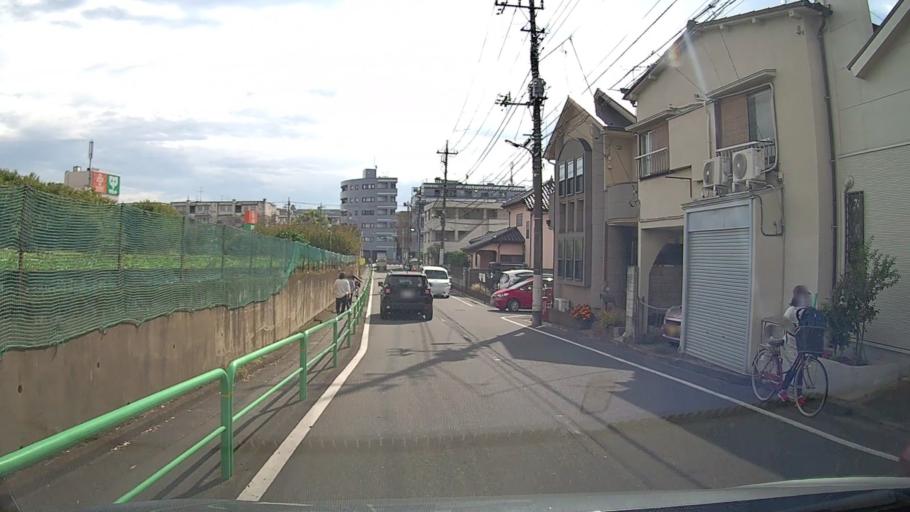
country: JP
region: Tokyo
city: Musashino
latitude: 35.7330
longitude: 139.5817
